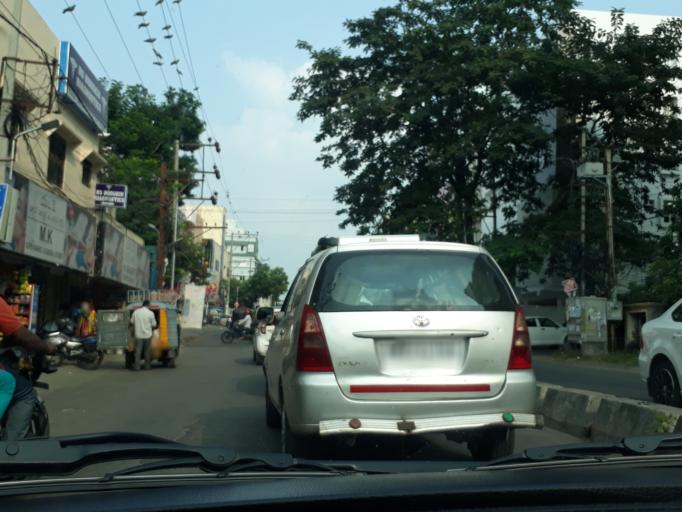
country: IN
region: Telangana
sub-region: Hyderabad
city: Hyderabad
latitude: 17.4302
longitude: 78.4377
